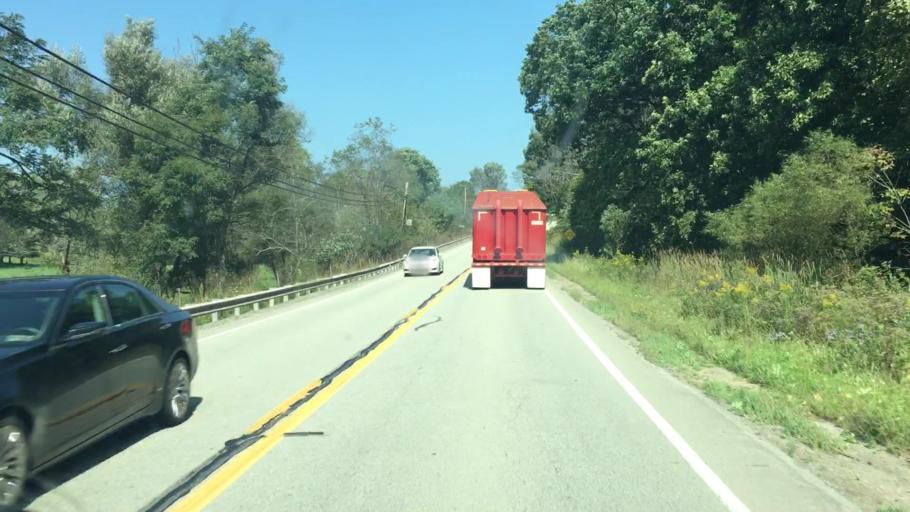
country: US
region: Pennsylvania
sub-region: Washington County
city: Washington
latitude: 40.0697
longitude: -80.2965
